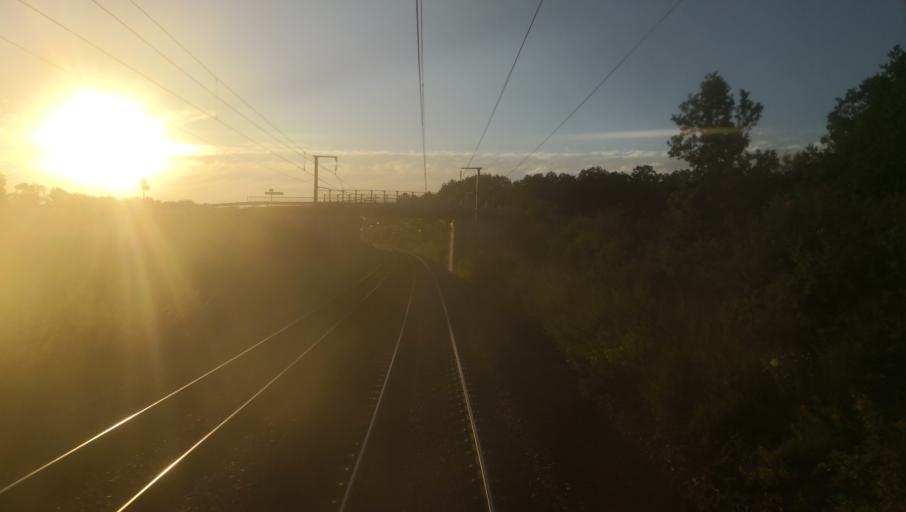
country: FR
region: Haute-Normandie
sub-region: Departement de l'Eure
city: Beaumont-le-Roger
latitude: 49.0161
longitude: 0.8354
